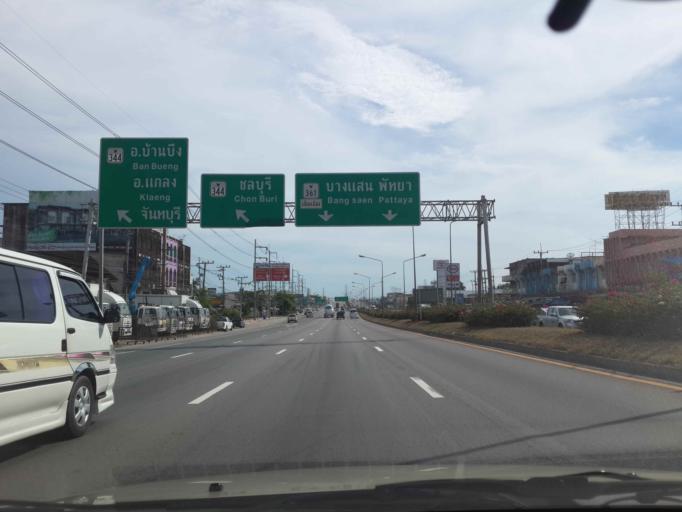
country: TH
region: Chon Buri
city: Chon Buri
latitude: 13.3573
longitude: 101.0103
